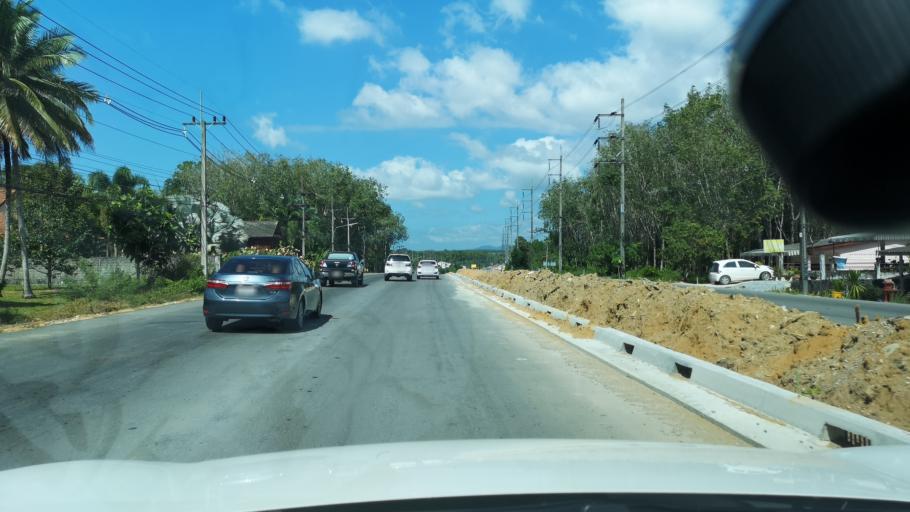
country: TH
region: Phangnga
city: Thai Mueang
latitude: 8.4385
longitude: 98.2569
